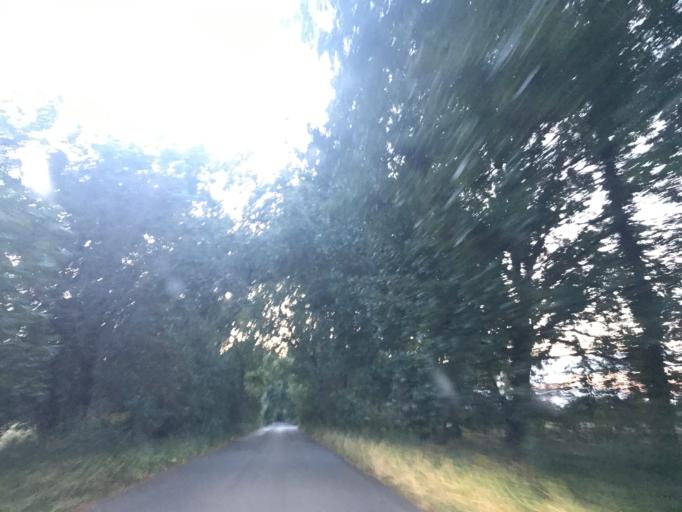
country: DE
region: Berlin
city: Gatow
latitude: 52.4821
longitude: 13.1637
